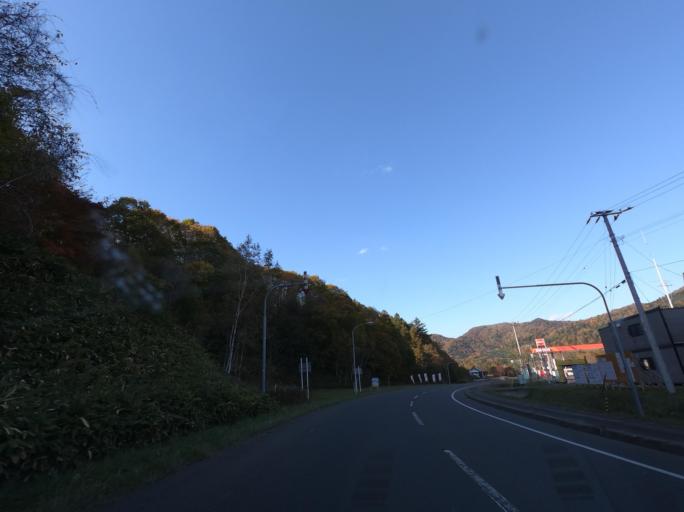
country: JP
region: Hokkaido
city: Iwamizawa
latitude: 43.0003
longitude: 142.0043
